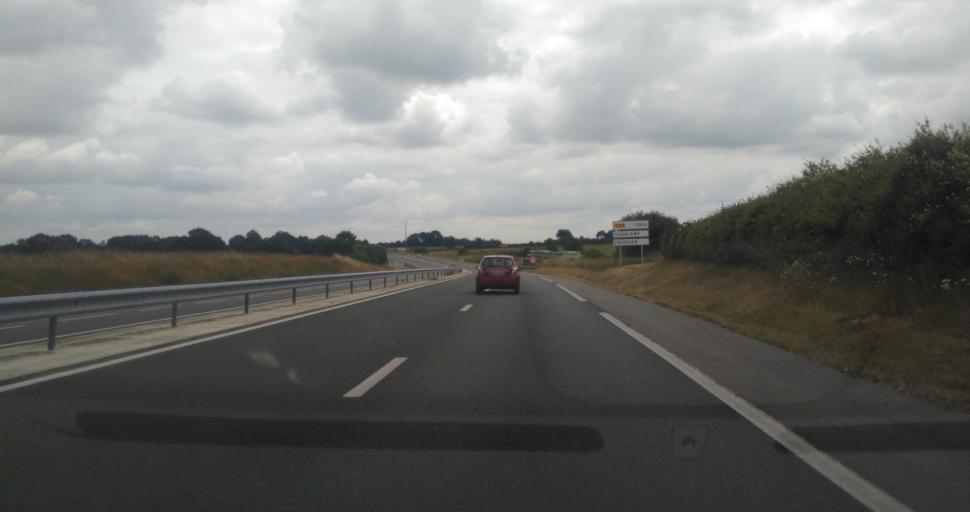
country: FR
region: Pays de la Loire
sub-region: Departement de la Vendee
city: La Chaize-le-Vicomte
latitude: 46.6580
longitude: -1.2436
